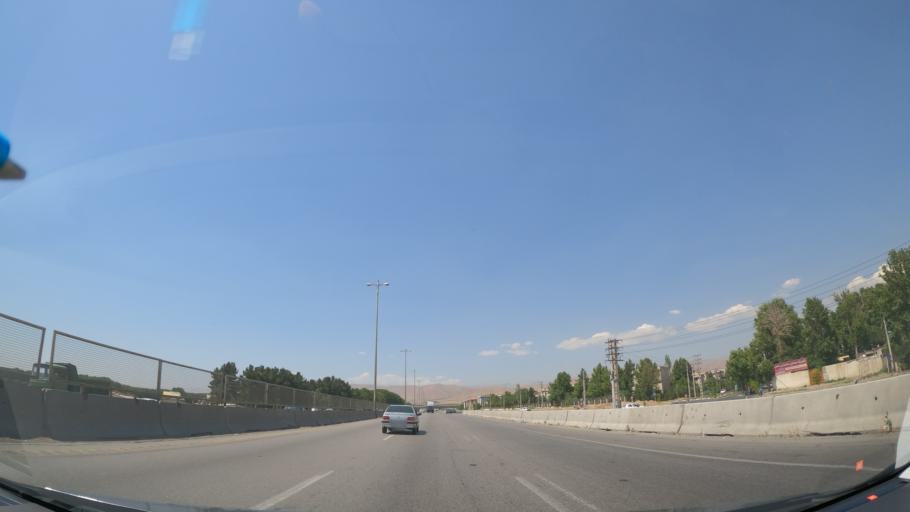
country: IR
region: Alborz
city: Karaj
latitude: 35.8415
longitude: 50.9097
